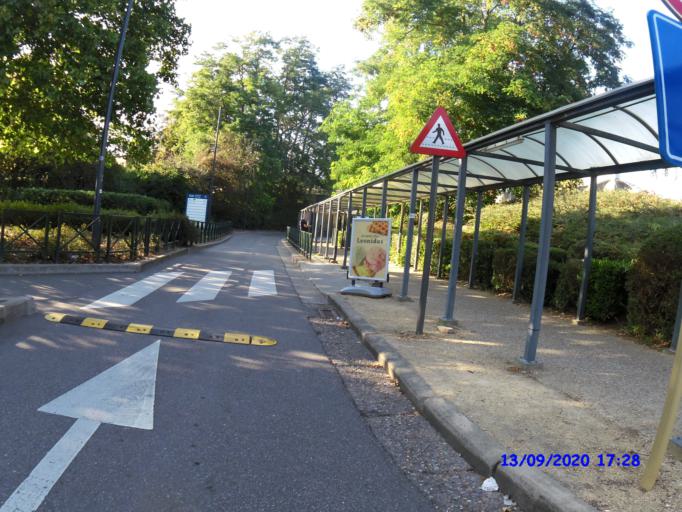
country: BE
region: Flanders
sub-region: Provincie Vlaams-Brabant
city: Dilbeek
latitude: 50.8146
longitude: 4.2663
